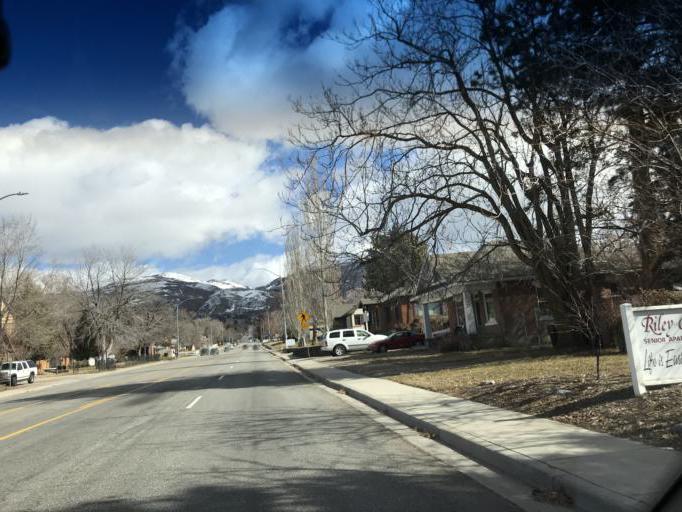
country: US
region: Utah
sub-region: Davis County
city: Bountiful
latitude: 40.8842
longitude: -111.8776
